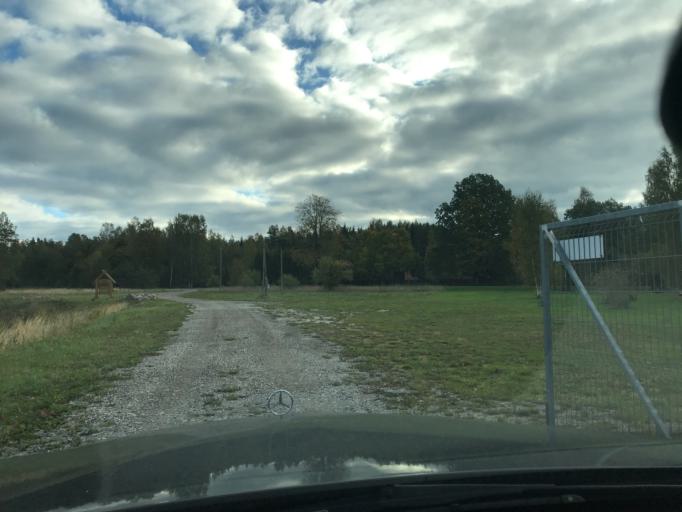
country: LV
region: Aloja
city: Staicele
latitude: 58.0969
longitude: 24.6848
